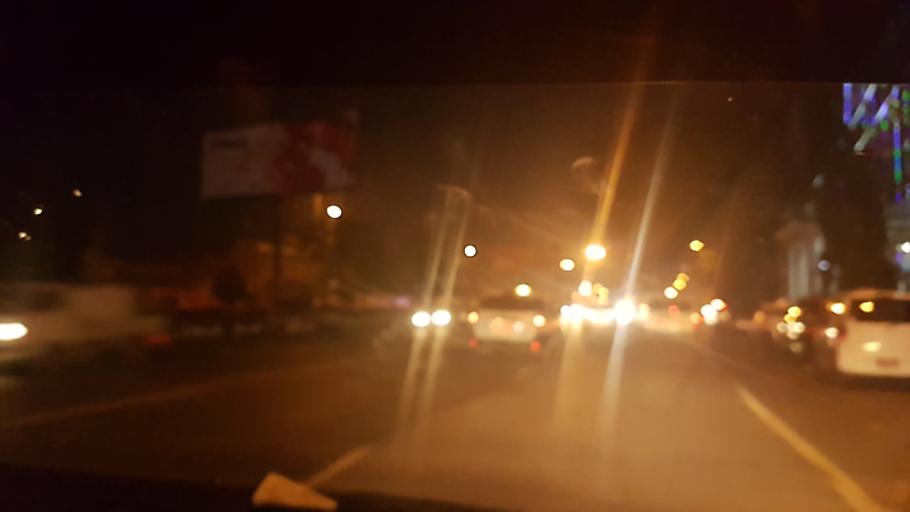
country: MM
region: Yangon
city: Yangon
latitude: 16.7695
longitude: 96.1609
